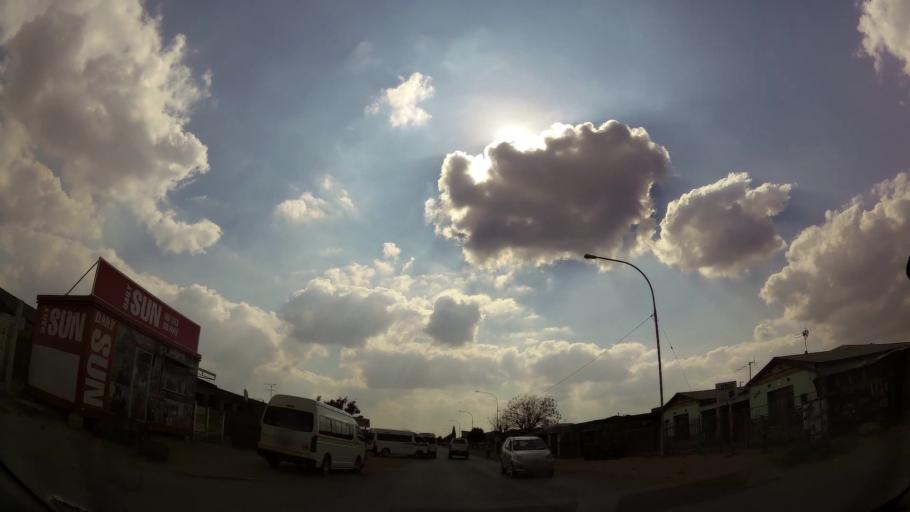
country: ZA
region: Gauteng
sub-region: Ekurhuleni Metropolitan Municipality
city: Brakpan
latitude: -26.1399
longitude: 28.4230
